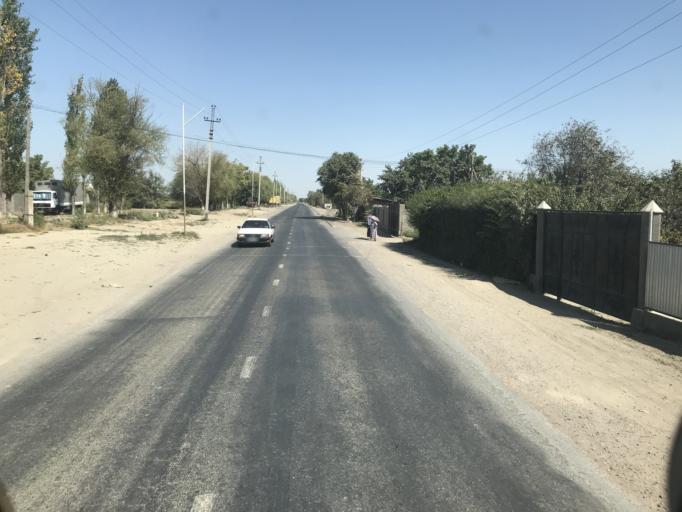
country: KZ
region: Ongtustik Qazaqstan
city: Ilyich
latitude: 40.9369
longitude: 68.4883
